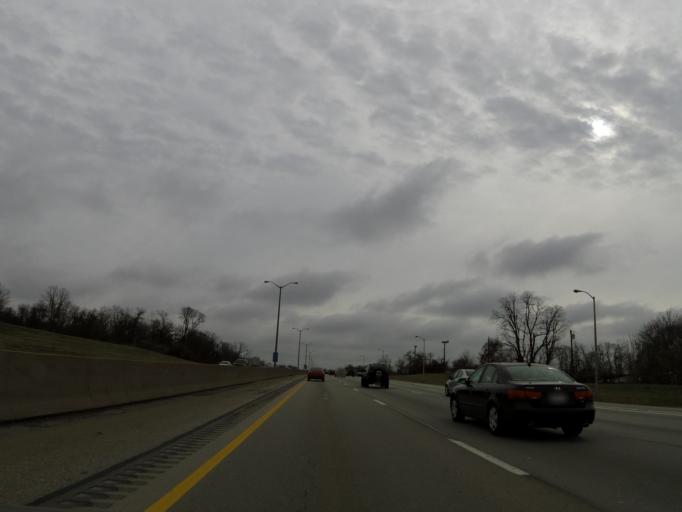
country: US
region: Kentucky
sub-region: Boone County
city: Florence
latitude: 38.9805
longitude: -84.6400
